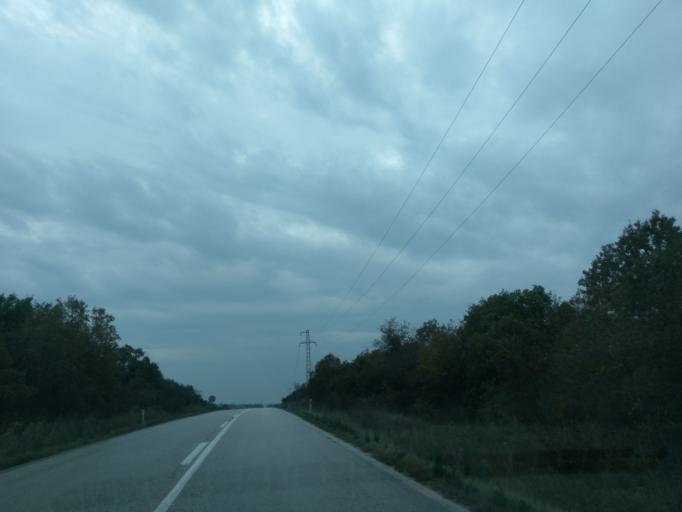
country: TR
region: Istanbul
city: Canta
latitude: 41.1553
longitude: 28.1068
